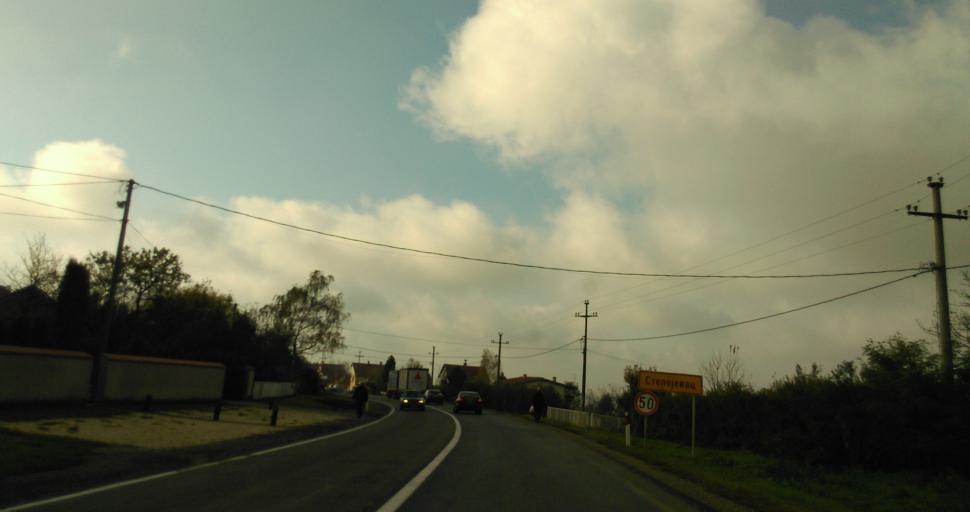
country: RS
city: Stepojevac
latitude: 44.5282
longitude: 20.2939
